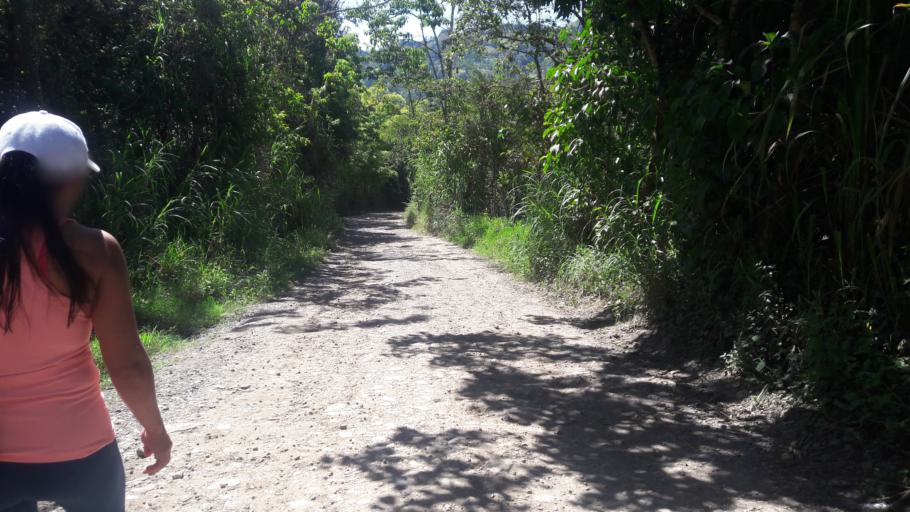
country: CO
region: Cundinamarca
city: Tenza
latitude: 5.0841
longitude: -73.4211
